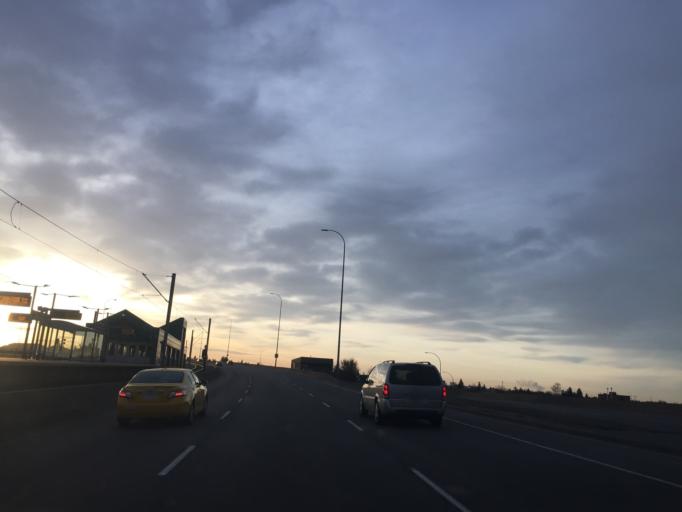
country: CA
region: Alberta
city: Calgary
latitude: 51.0455
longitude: -114.0075
